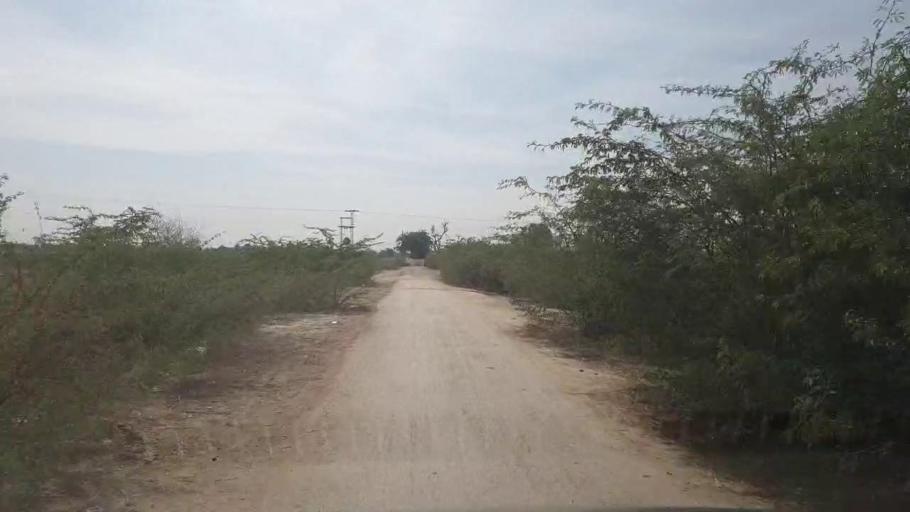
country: PK
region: Sindh
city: Umarkot
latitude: 25.2715
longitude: 69.7063
